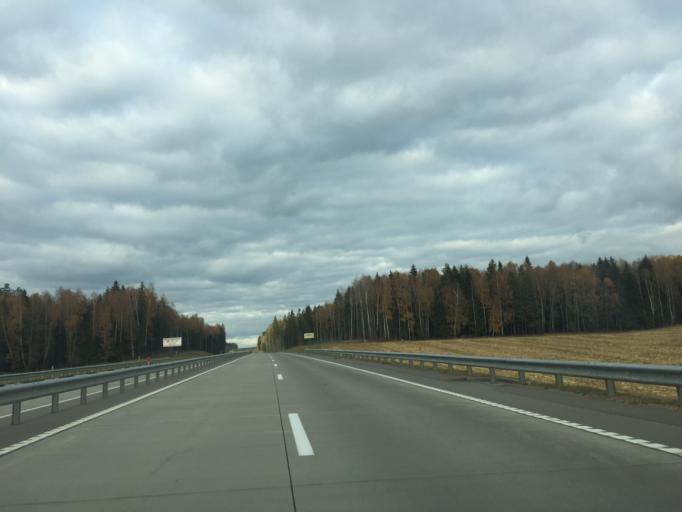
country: BY
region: Minsk
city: Rakaw
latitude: 54.0077
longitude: 27.1304
